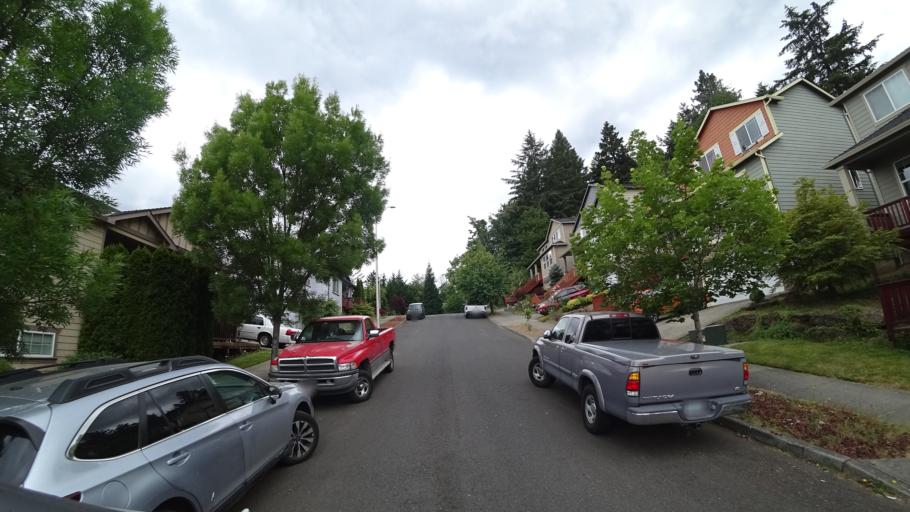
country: US
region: Oregon
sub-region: Clackamas County
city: Happy Valley
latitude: 45.4857
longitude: -122.5174
